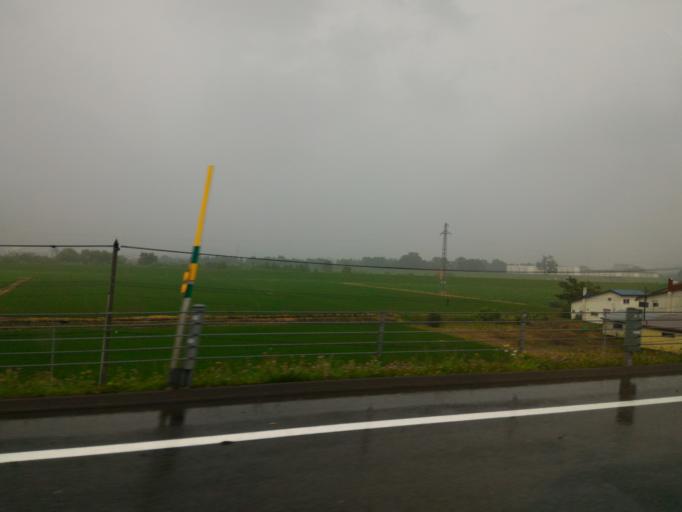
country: JP
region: Hokkaido
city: Nayoro
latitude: 44.3600
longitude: 142.4359
